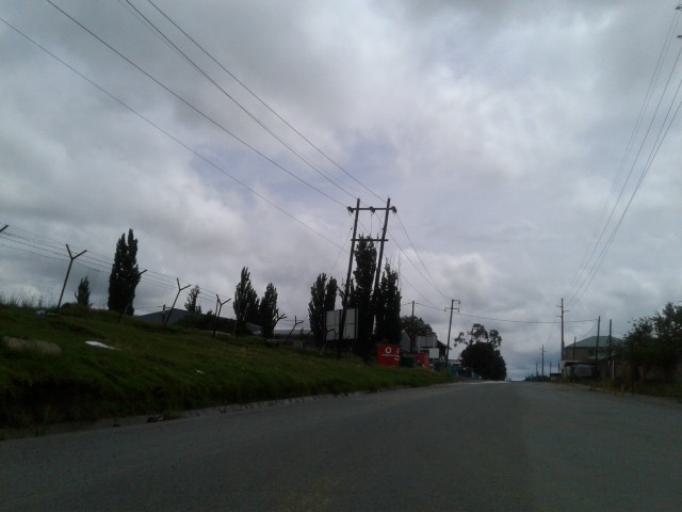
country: LS
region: Maseru
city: Maseru
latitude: -29.2969
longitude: 27.4792
